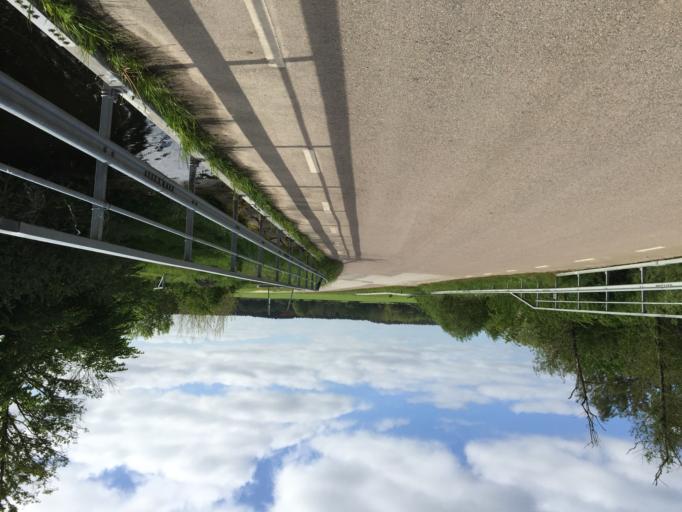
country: SE
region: Skane
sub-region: Sjobo Kommun
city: Blentarp
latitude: 55.6691
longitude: 13.6237
